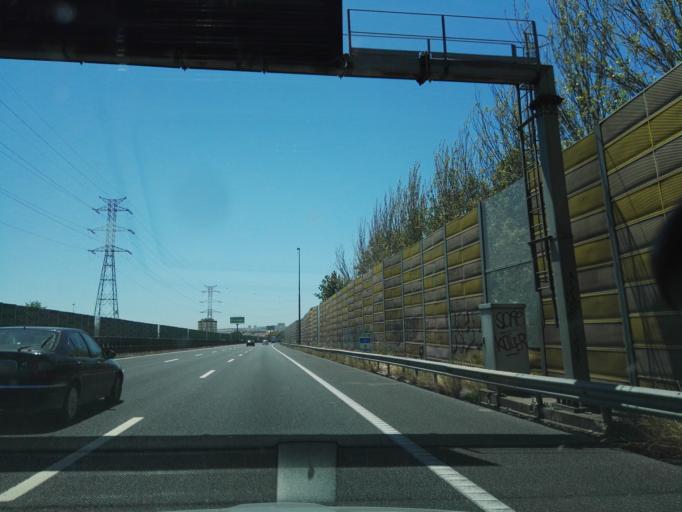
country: PT
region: Lisbon
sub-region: Loures
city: Bobadela
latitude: 38.8151
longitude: -9.1015
